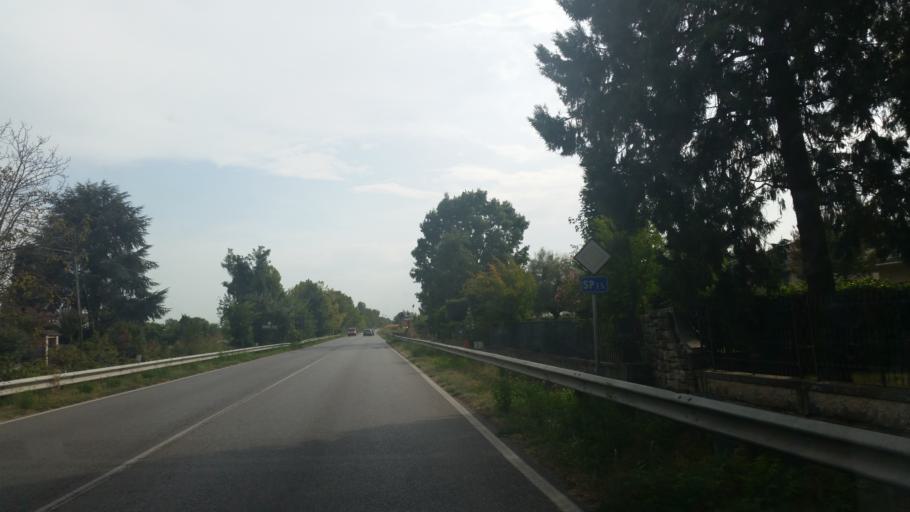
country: IT
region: Lombardy
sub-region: Provincia di Brescia
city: Dello
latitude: 45.4156
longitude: 10.0795
